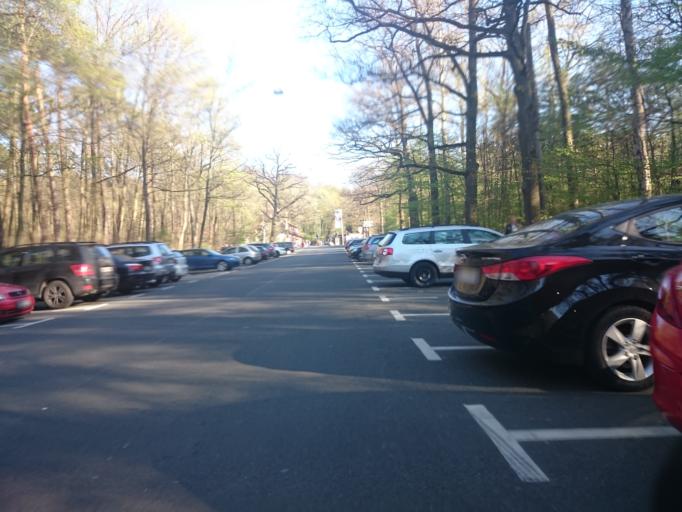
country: DE
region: Bavaria
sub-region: Regierungsbezirk Mittelfranken
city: Nuernberg
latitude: 49.4515
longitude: 11.1379
